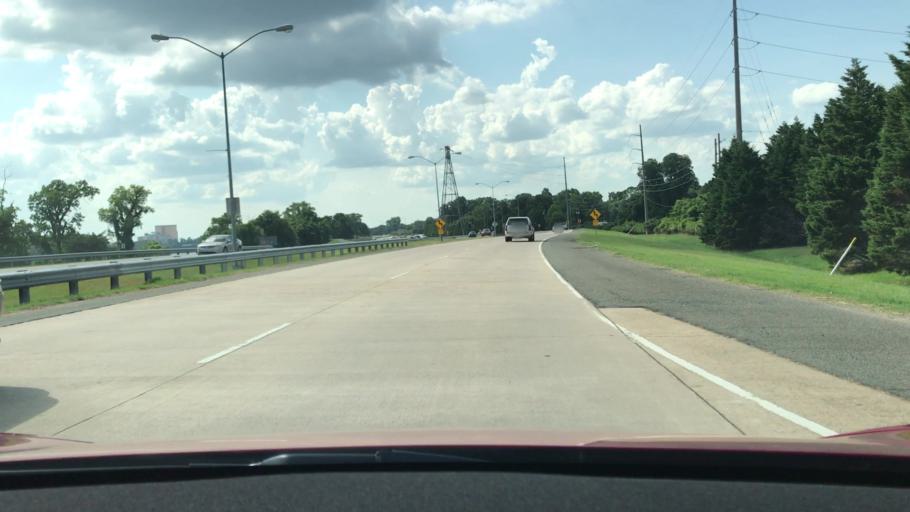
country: US
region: Louisiana
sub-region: Bossier Parish
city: Bossier City
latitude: 32.5017
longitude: -93.7056
